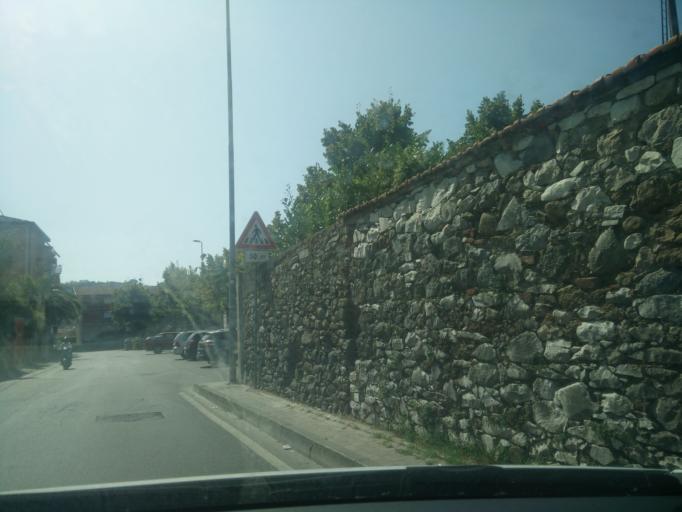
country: IT
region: Tuscany
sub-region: Provincia di Massa-Carrara
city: Carrara
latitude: 44.0611
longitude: 10.0843
